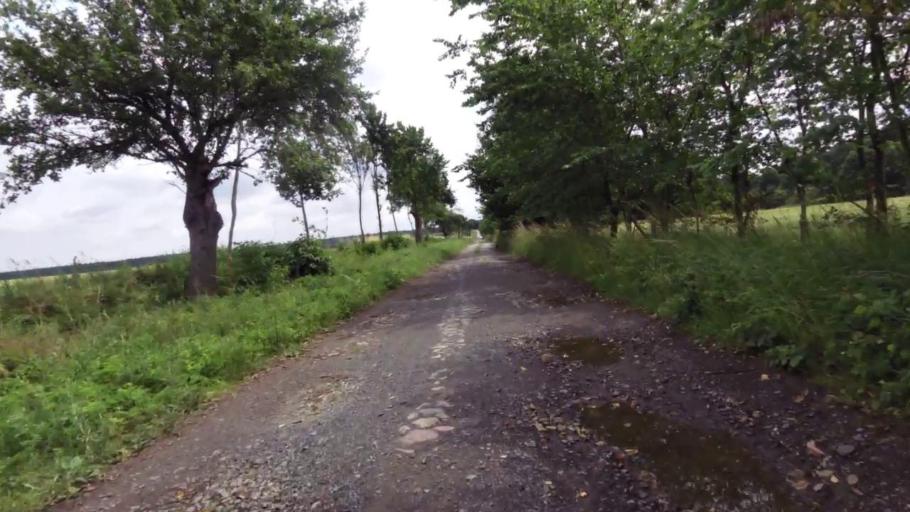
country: PL
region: West Pomeranian Voivodeship
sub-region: Powiat mysliborski
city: Mysliborz
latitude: 52.9761
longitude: 14.8952
